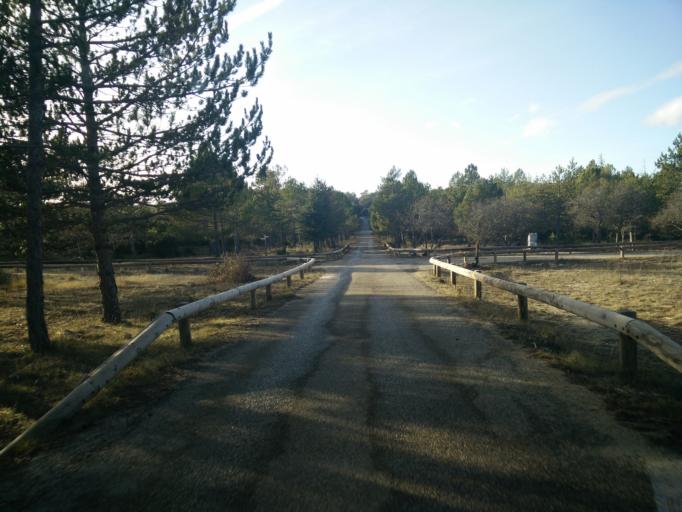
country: FR
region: Provence-Alpes-Cote d'Azur
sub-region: Departement du Var
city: Le Revest-les-Eaux
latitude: 43.2271
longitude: 5.9216
